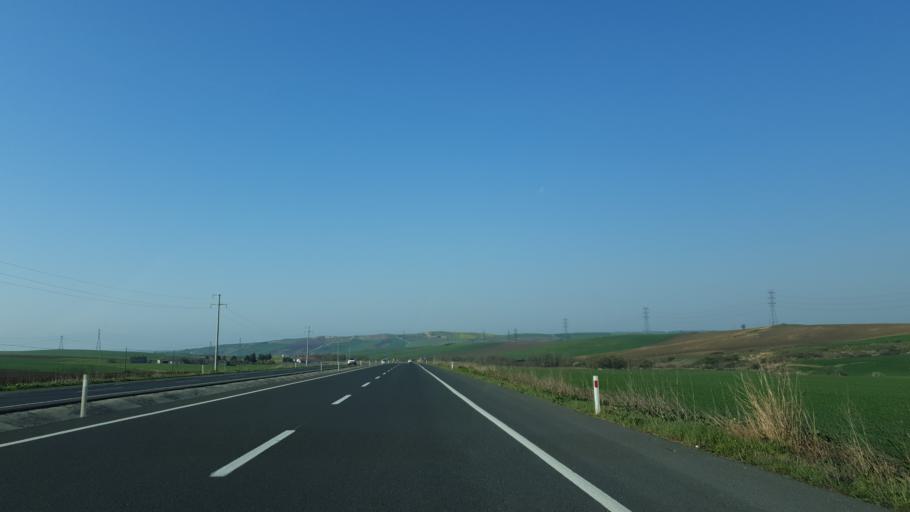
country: TR
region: Tekirdag
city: Corlu
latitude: 41.0905
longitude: 27.7466
